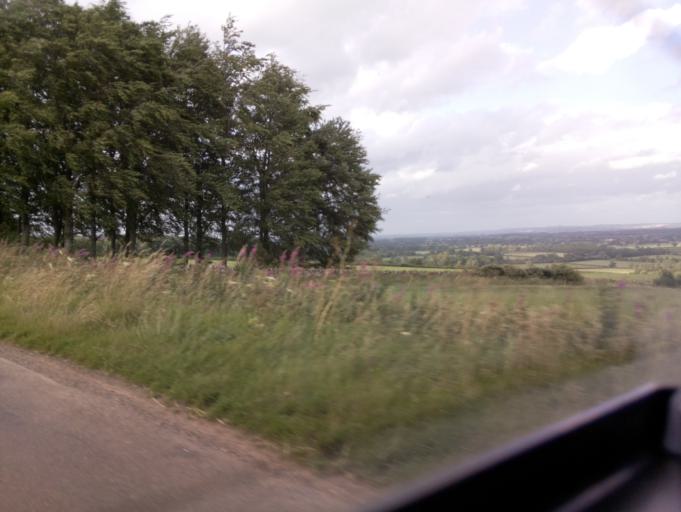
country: GB
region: England
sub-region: Gloucestershire
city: Donnington
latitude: 51.9671
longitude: -1.7509
